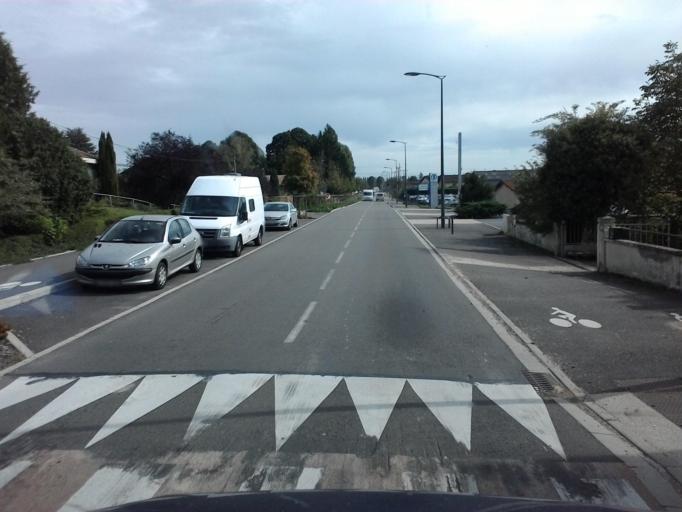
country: FR
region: Rhone-Alpes
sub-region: Departement de l'Ain
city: Replonges
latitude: 46.3006
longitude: 4.8749
